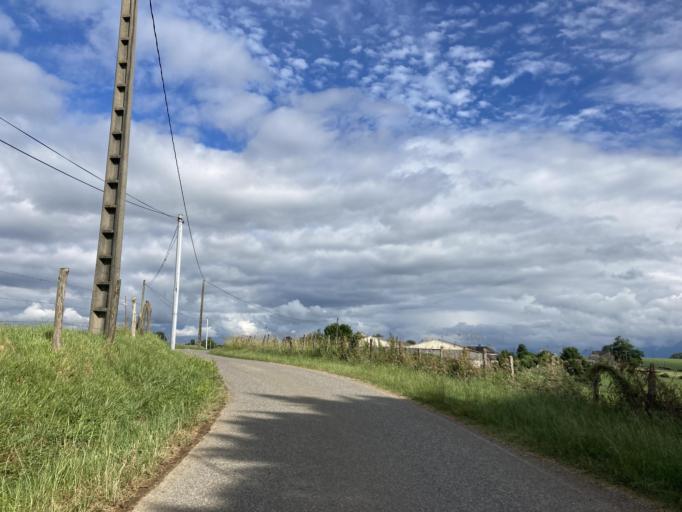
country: FR
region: Aquitaine
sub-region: Departement des Pyrenees-Atlantiques
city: Ledeuix
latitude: 43.2534
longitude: -0.6240
